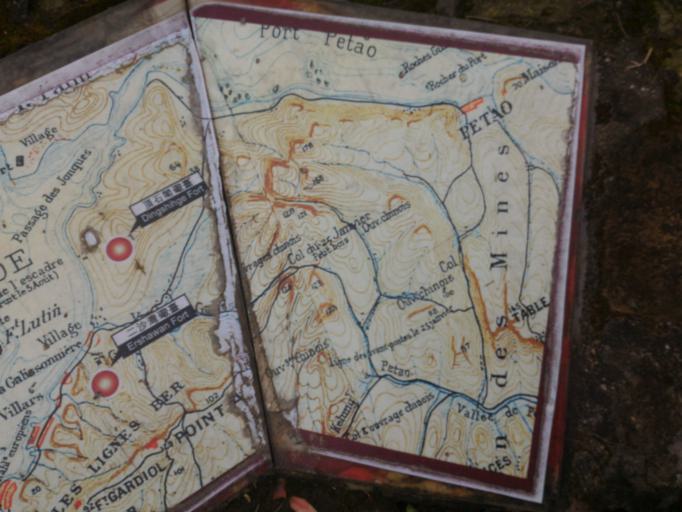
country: TW
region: Taiwan
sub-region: Keelung
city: Keelung
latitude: 25.1399
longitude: 121.7568
